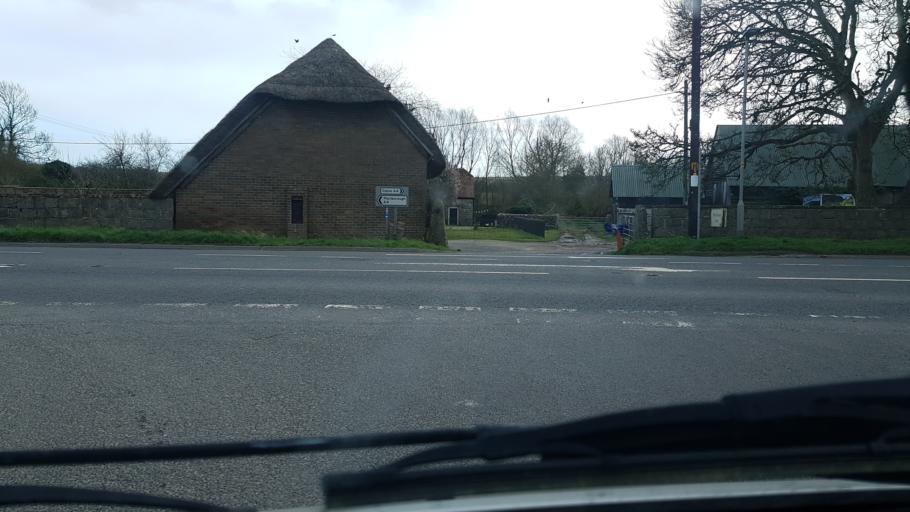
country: GB
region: England
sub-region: Wiltshire
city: Avebury
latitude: 51.4144
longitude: -1.8408
